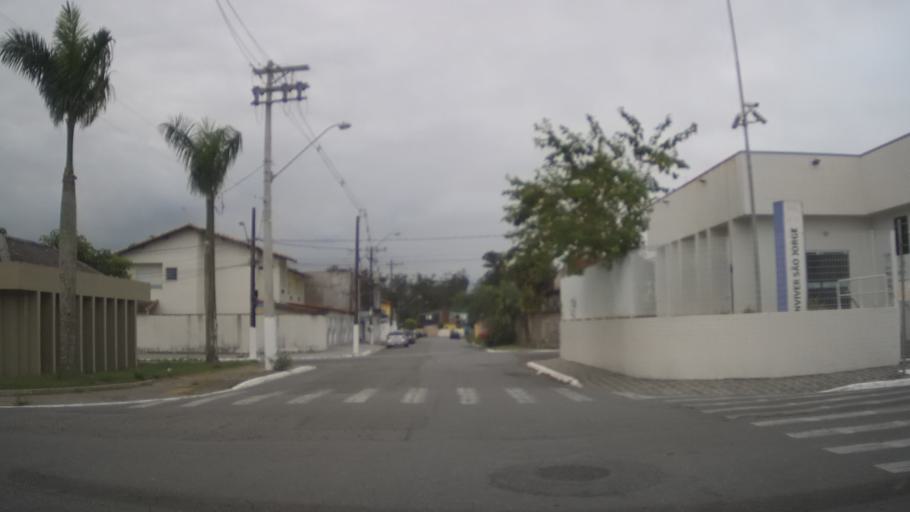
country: BR
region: Sao Paulo
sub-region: Praia Grande
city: Praia Grande
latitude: -24.0083
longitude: -46.4558
